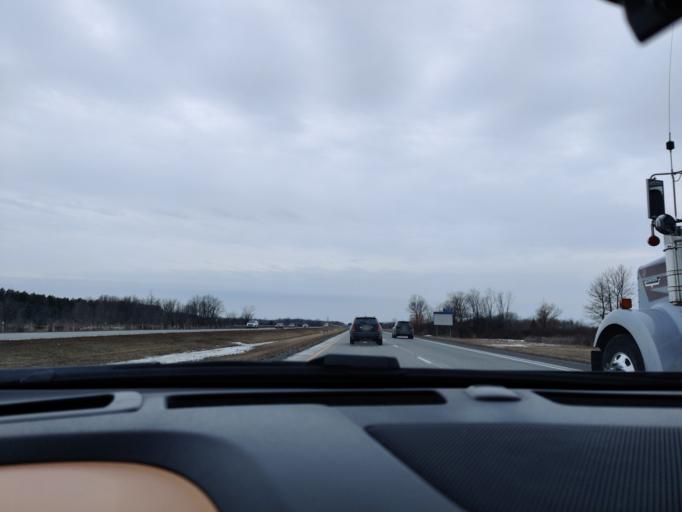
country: US
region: New York
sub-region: St. Lawrence County
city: Norfolk
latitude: 44.9595
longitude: -75.0945
